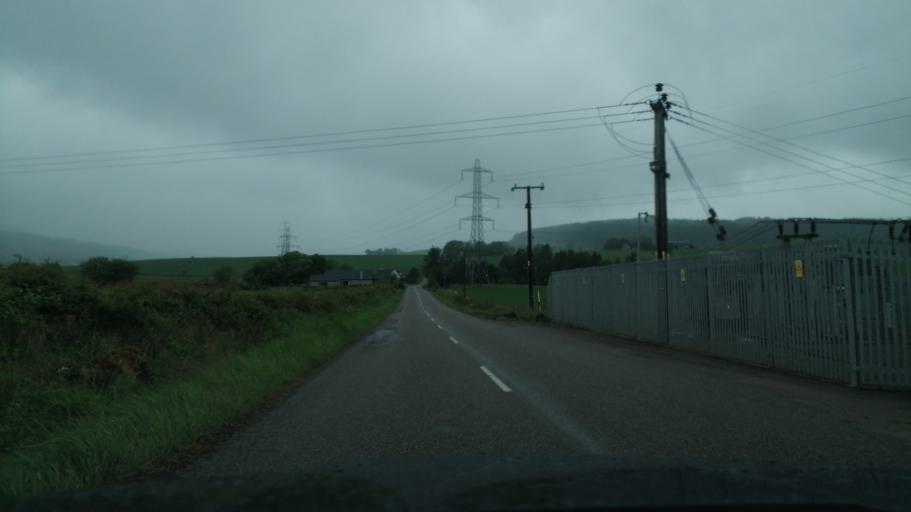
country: GB
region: Scotland
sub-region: Aberdeenshire
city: Huntly
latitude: 57.5436
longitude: -2.8014
